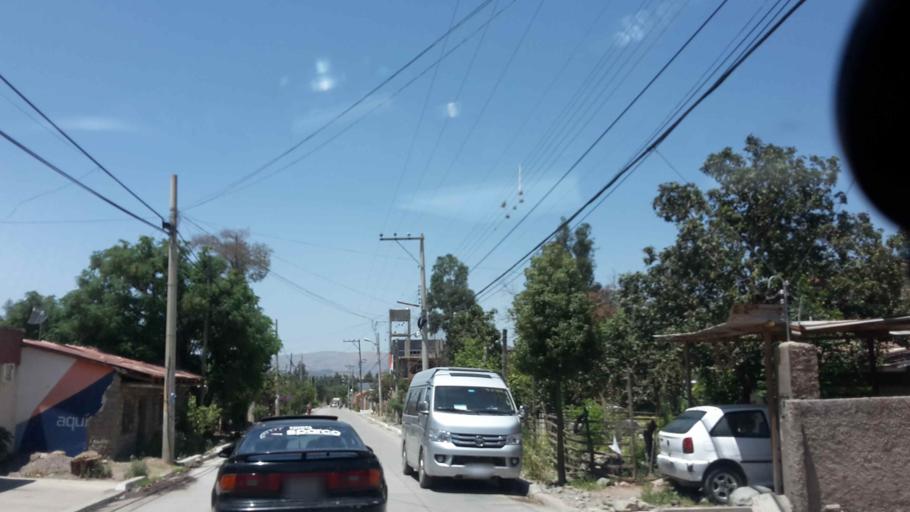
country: BO
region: Cochabamba
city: Cochabamba
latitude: -17.3504
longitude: -66.2060
